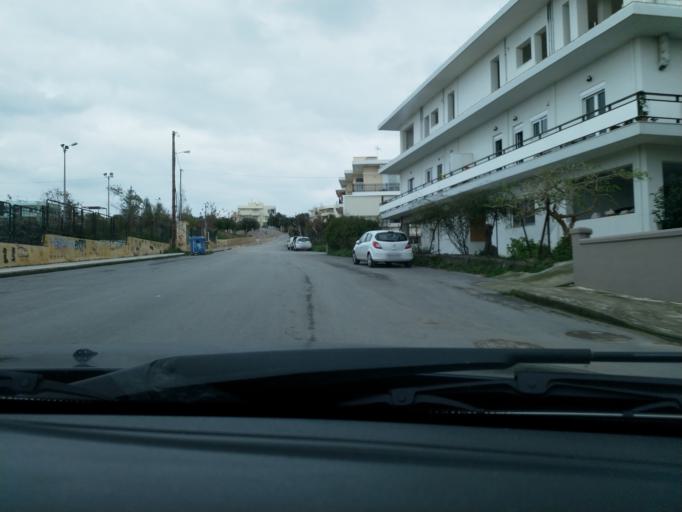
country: GR
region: Crete
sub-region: Nomos Chanias
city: Chania
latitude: 35.5117
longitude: 24.0366
